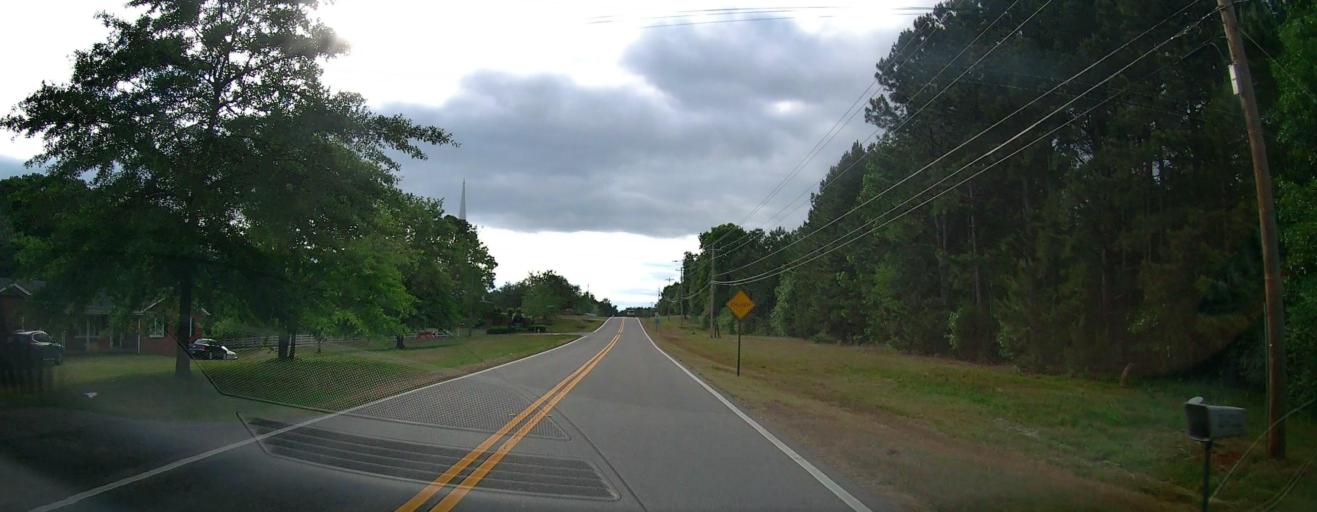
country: US
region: Georgia
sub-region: Oconee County
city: Watkinsville
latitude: 33.9074
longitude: -83.4686
